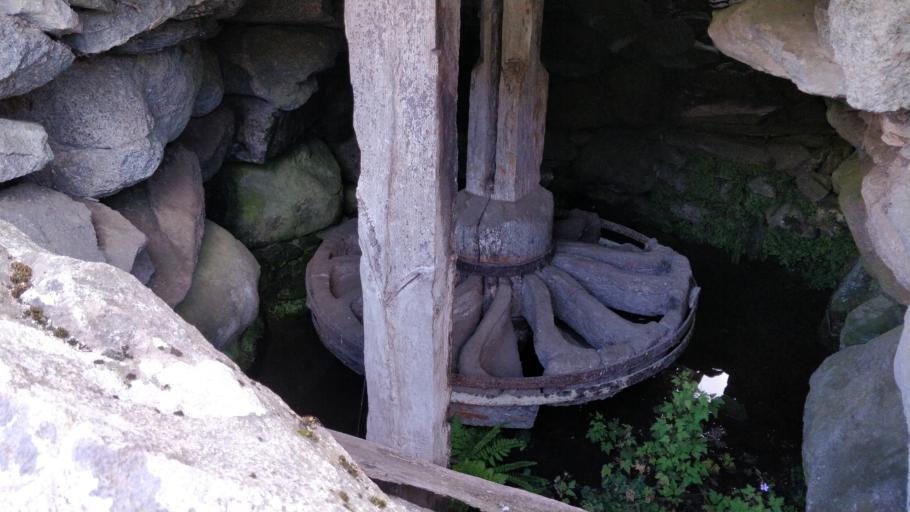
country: FR
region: Midi-Pyrenees
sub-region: Departement des Hautes-Pyrenees
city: Luz-Saint-Sauveur
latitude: 42.8845
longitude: -0.0260
